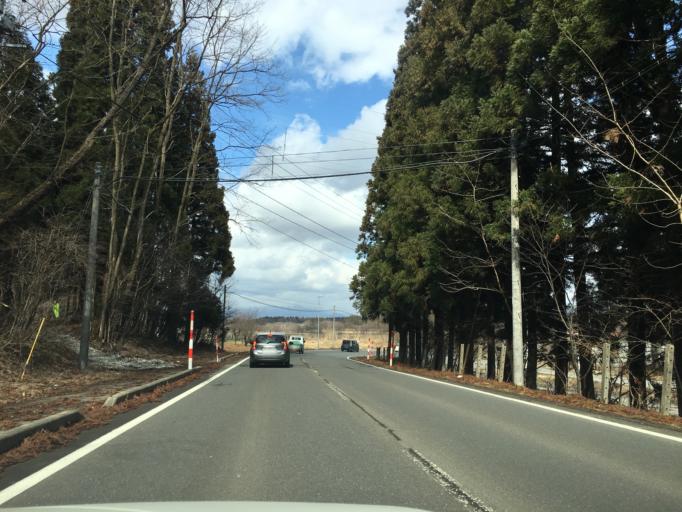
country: JP
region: Akita
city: Odate
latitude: 40.2030
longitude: 140.5554
